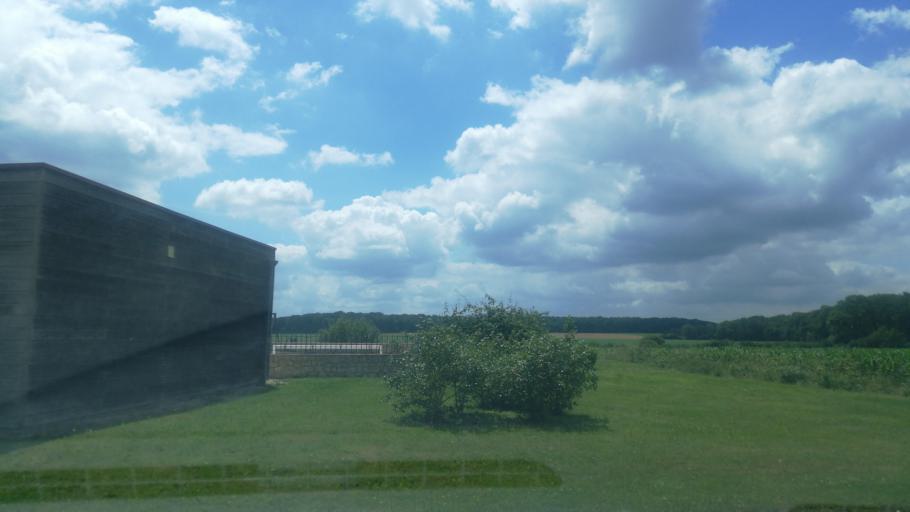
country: FR
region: Centre
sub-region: Departement du Loir-et-Cher
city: Contres
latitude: 47.3635
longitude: 1.4555
